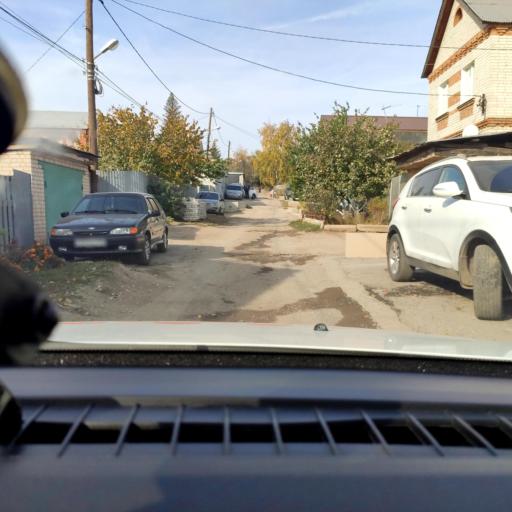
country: RU
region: Samara
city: Samara
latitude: 53.1827
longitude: 50.1795
